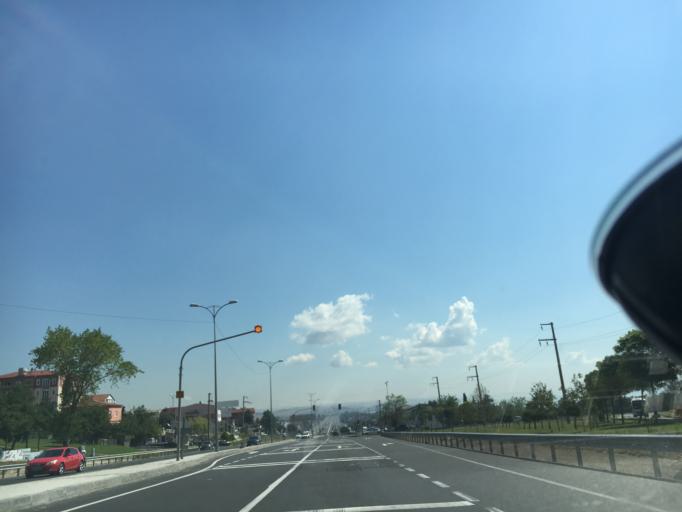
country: TR
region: Tekirdag
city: Sultankoy
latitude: 41.0468
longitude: 28.0439
